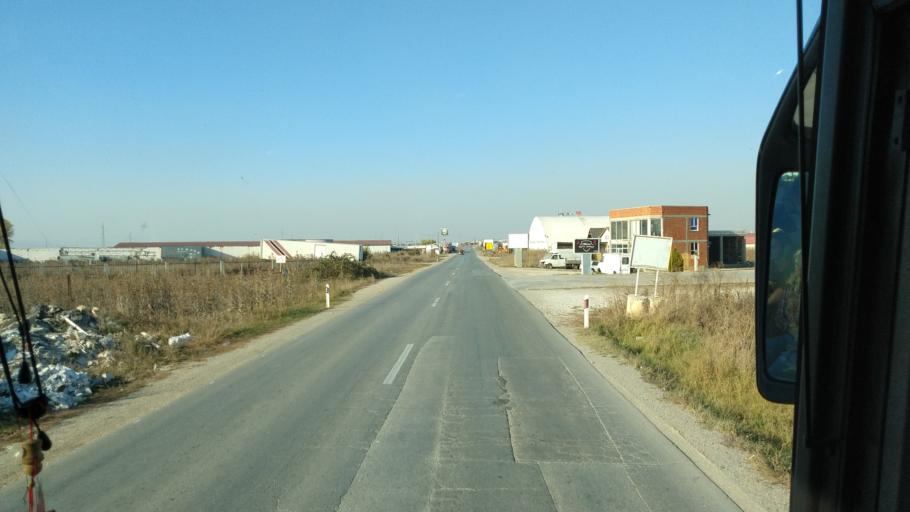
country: XK
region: Pristina
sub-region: Lipjan
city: Lipljan
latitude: 42.5176
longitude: 21.1125
